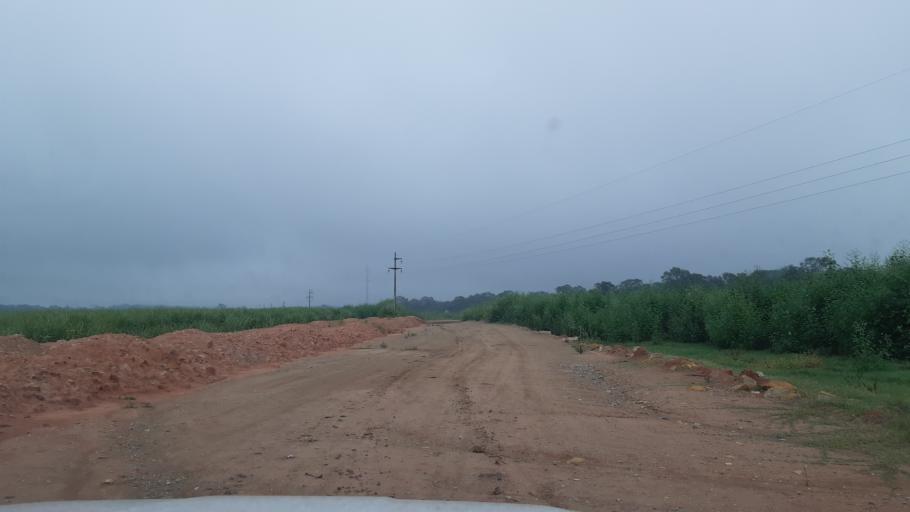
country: AR
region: Jujuy
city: La Mendieta
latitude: -24.3758
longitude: -65.0035
